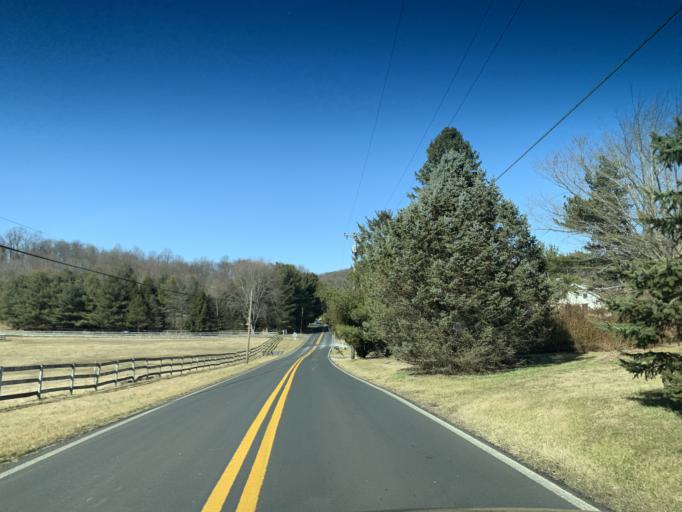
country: US
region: Maryland
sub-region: Carroll County
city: Manchester
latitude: 39.6229
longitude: -76.8917
